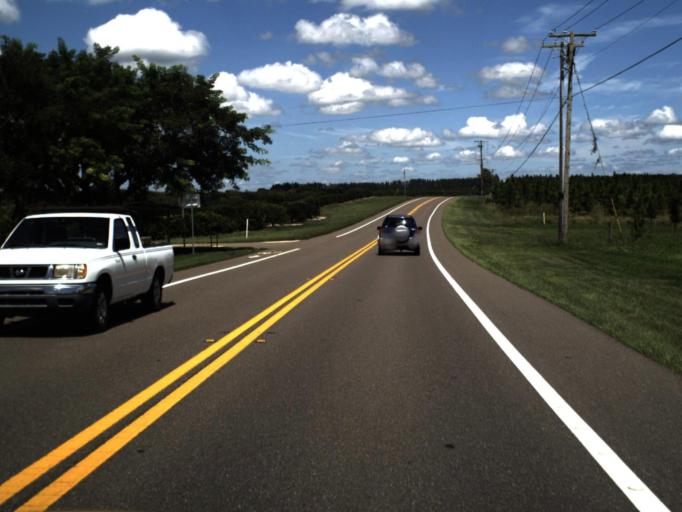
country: US
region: Florida
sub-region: Polk County
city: Crooked Lake Park
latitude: 27.8570
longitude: -81.5729
